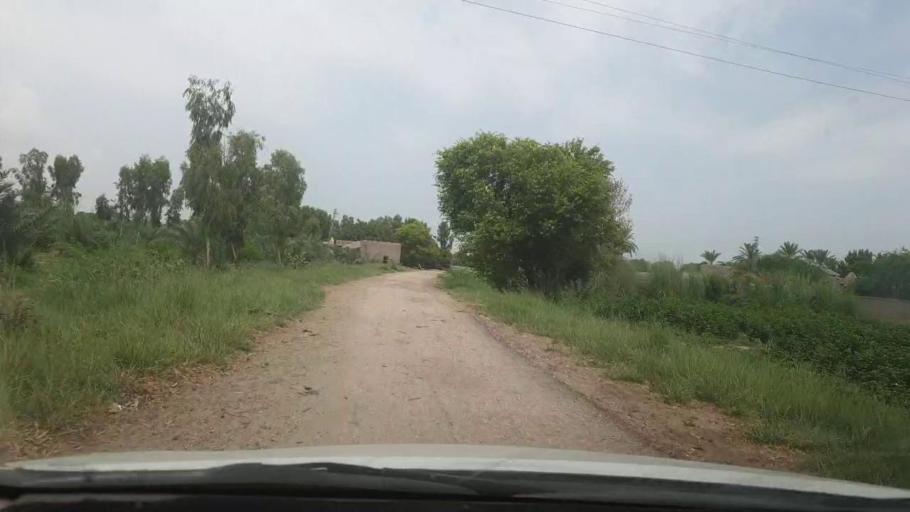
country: PK
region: Sindh
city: Khairpur
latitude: 27.3726
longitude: 68.9853
